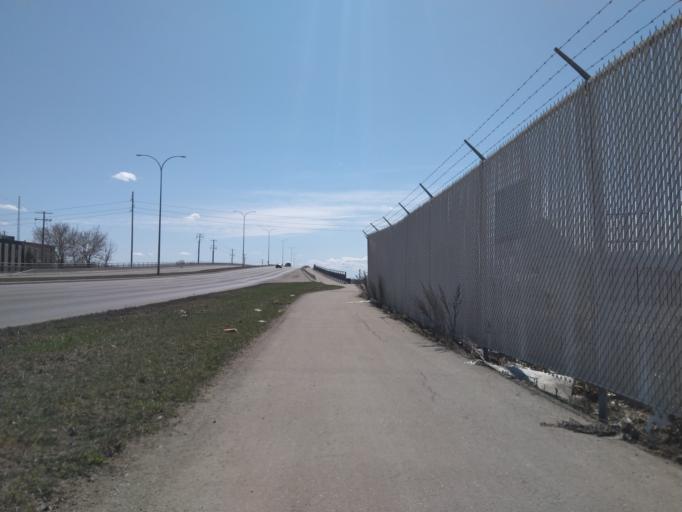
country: CA
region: Alberta
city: Calgary
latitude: 50.9666
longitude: -113.9588
